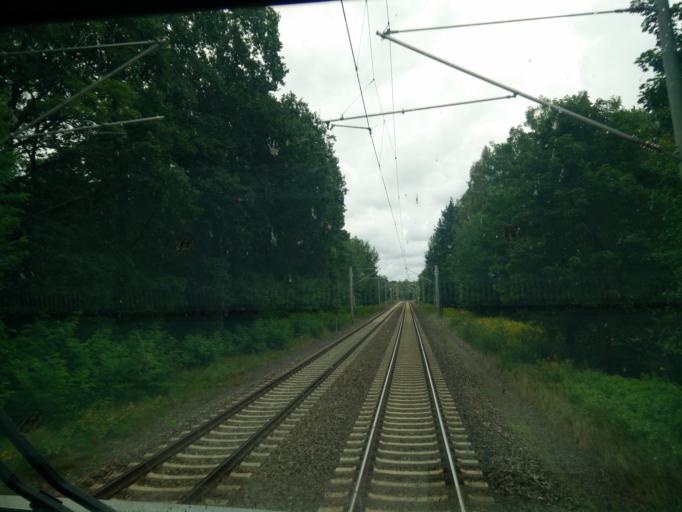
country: DE
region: Brandenburg
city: Schwerin
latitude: 52.1854
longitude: 13.6321
